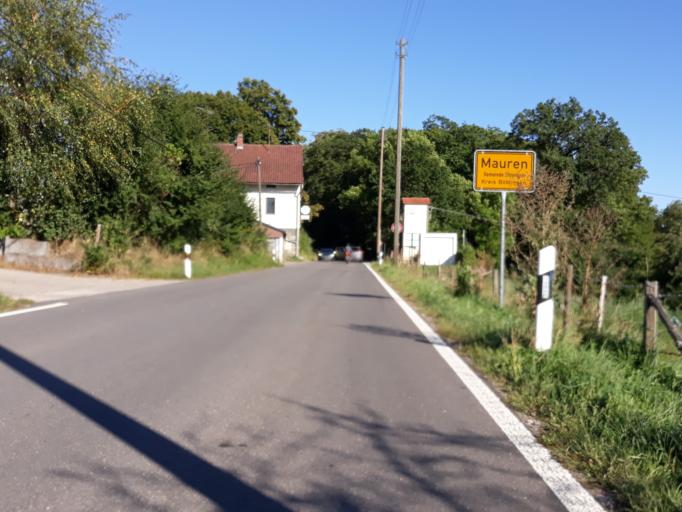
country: DE
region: Baden-Wuerttemberg
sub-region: Regierungsbezirk Stuttgart
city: Hildrizhausen
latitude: 48.6508
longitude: 8.9755
